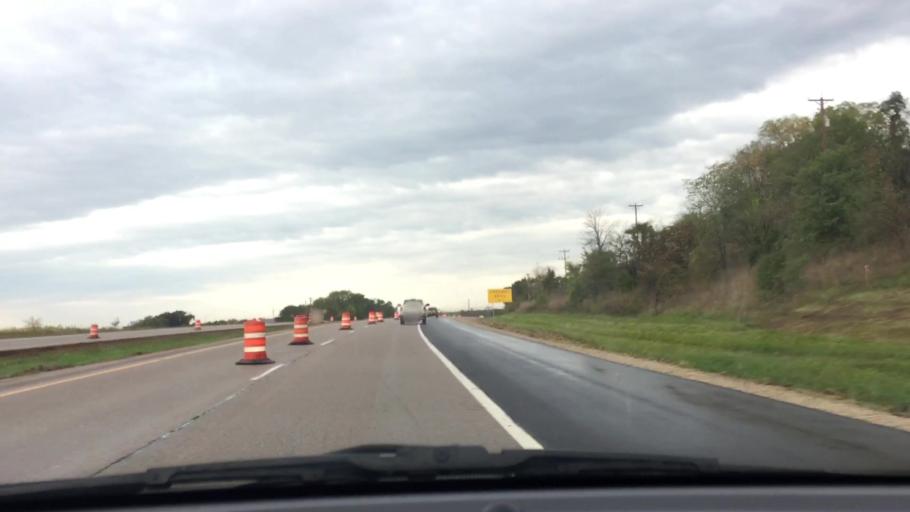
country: US
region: Wisconsin
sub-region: Rock County
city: Beloit
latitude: 42.5331
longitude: -88.9601
